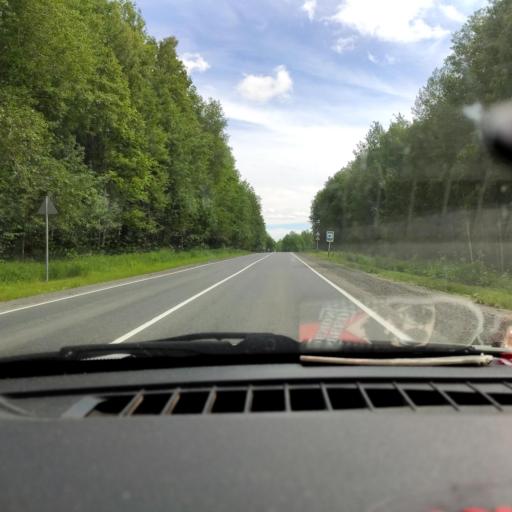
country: RU
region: Perm
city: Chusovoy
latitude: 58.3840
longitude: 57.9249
